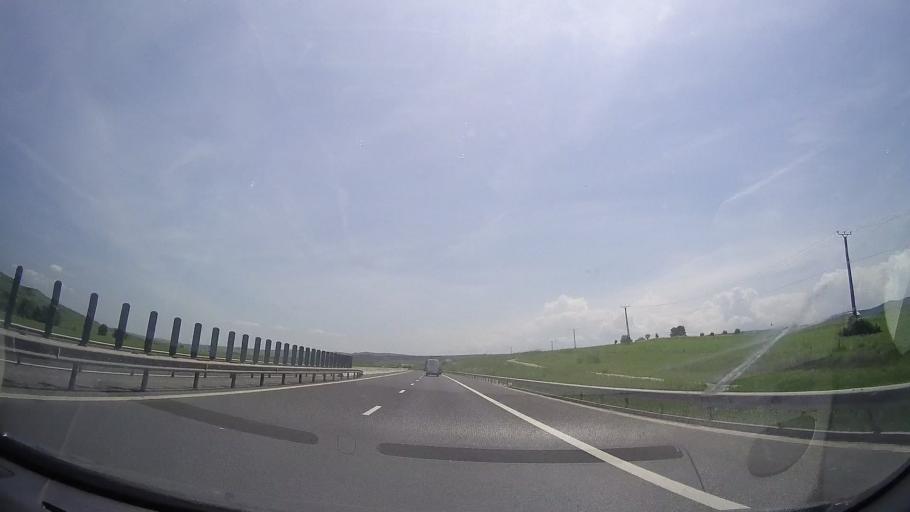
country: RO
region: Alba
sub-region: Municipiul Sebes
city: Sebes
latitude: 45.9306
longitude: 23.6087
